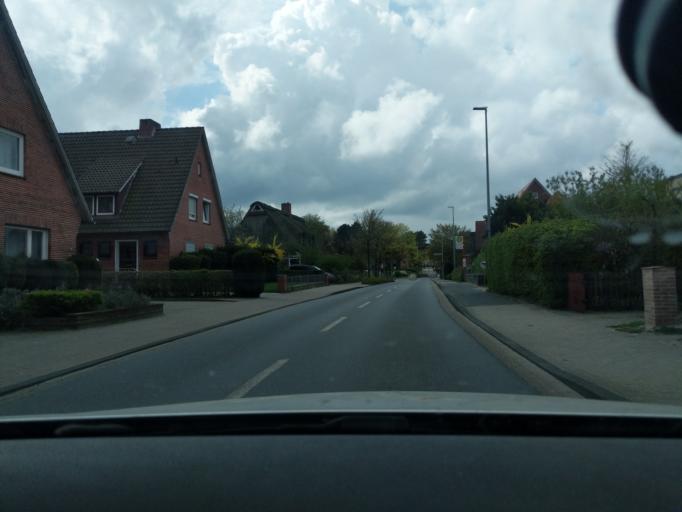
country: DE
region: Lower Saxony
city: Stade
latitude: 53.5885
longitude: 9.4654
